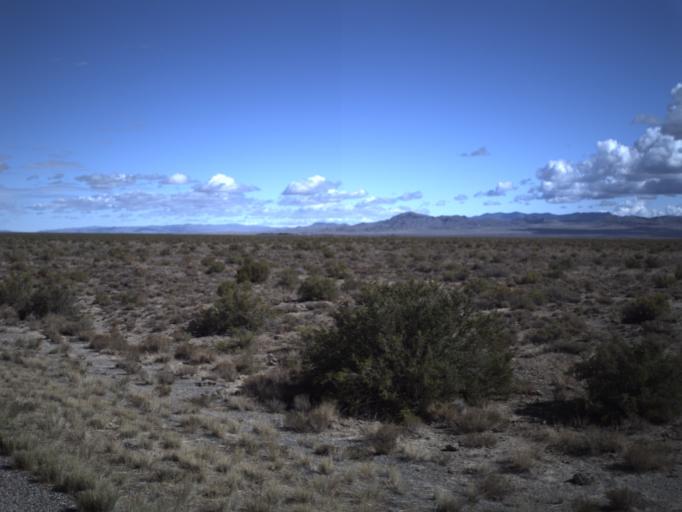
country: US
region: Nevada
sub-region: White Pine County
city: McGill
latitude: 39.0003
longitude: -114.0348
